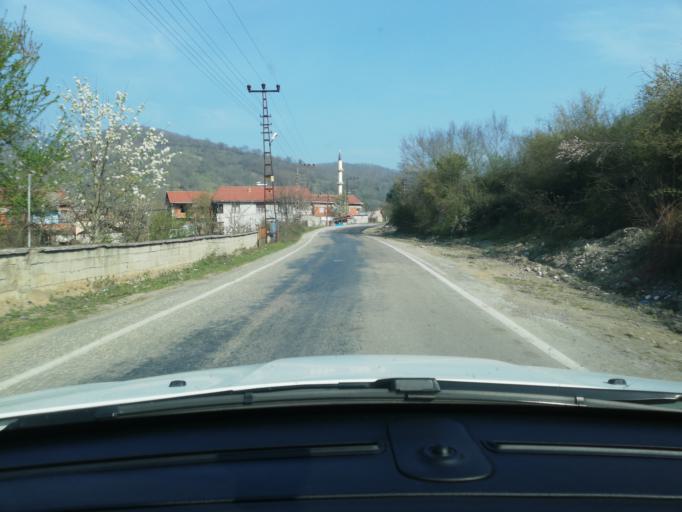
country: TR
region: Karabuk
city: Yenice
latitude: 41.2429
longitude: 32.3565
